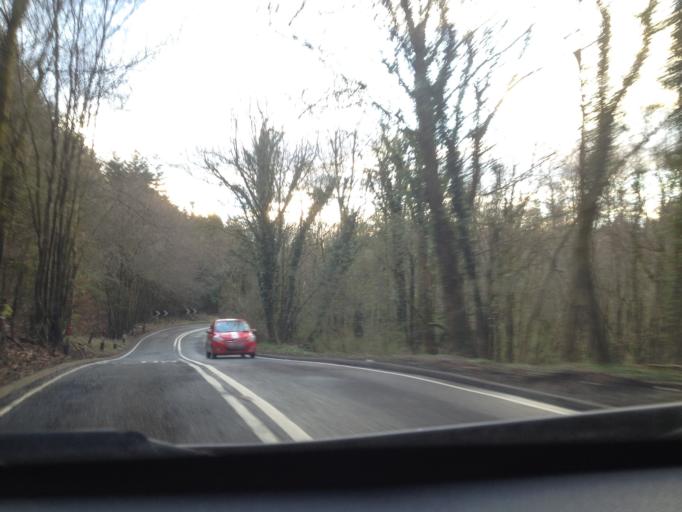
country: GB
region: Scotland
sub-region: South Lanarkshire
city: Dalserf
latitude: 55.7416
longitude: -3.9111
